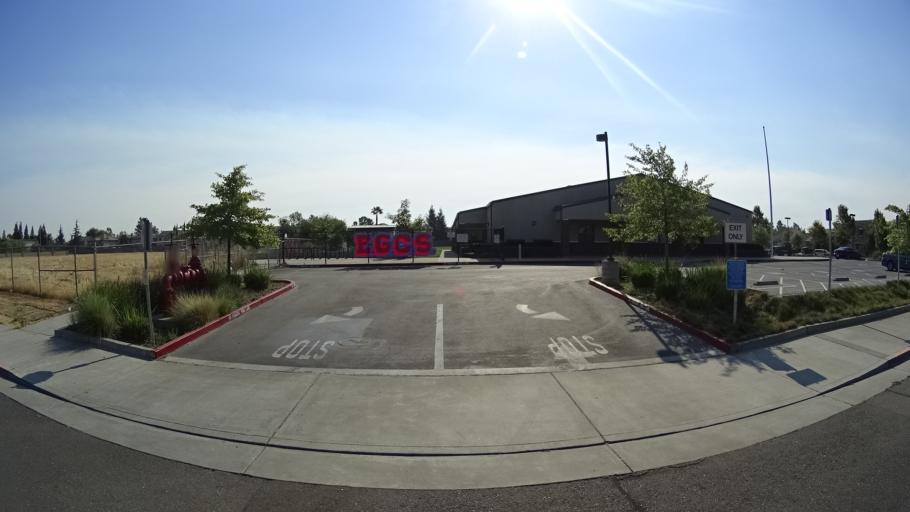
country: US
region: California
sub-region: Sacramento County
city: Laguna
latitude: 38.3916
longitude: -121.4378
